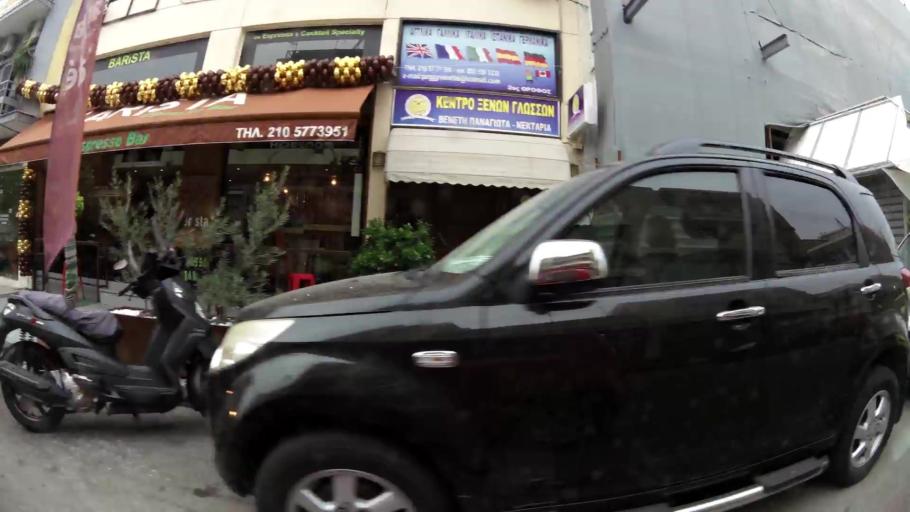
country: GR
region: Attica
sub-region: Nomarchia Athinas
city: Peristeri
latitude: 38.0112
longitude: 23.6980
